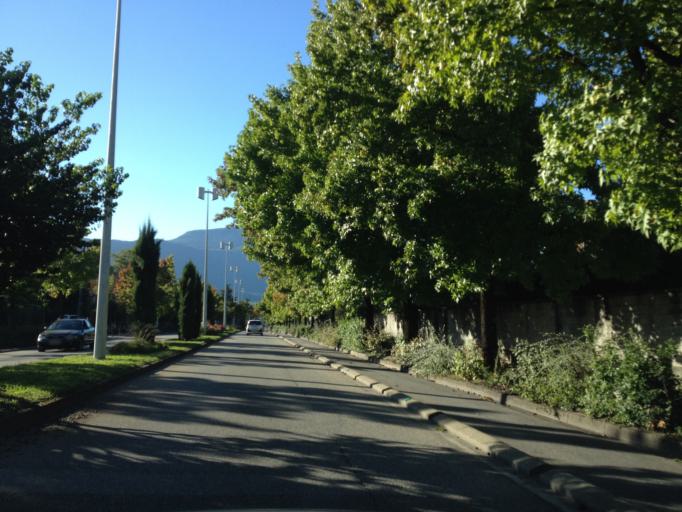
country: FR
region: Rhone-Alpes
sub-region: Departement de la Savoie
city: Cognin
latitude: 45.5748
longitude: 5.9022
